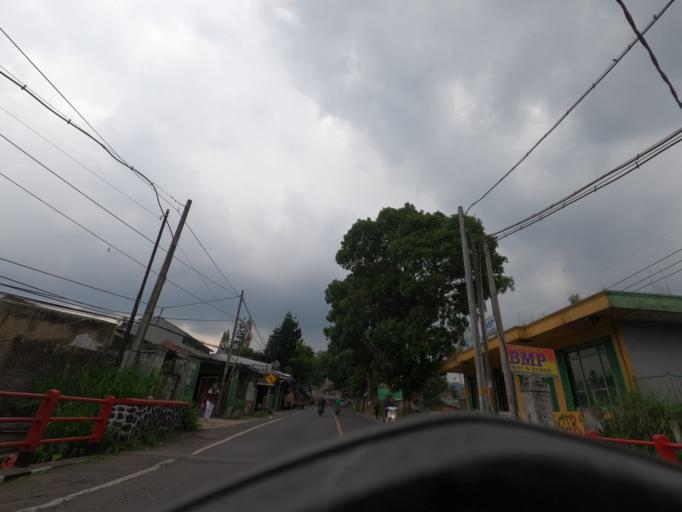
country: ID
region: West Java
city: Sukabumi
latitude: -6.7770
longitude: 107.0635
